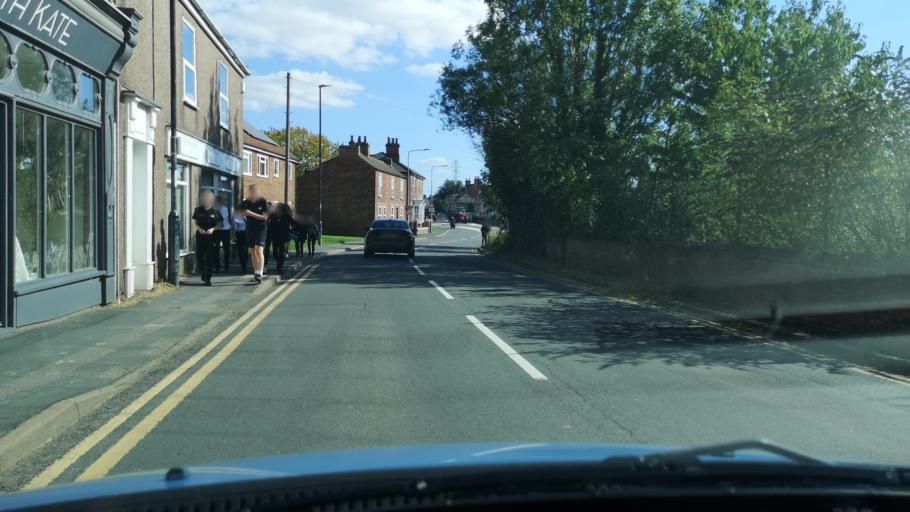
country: GB
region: England
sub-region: North Lincolnshire
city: Crowle
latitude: 53.6050
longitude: -0.8327
